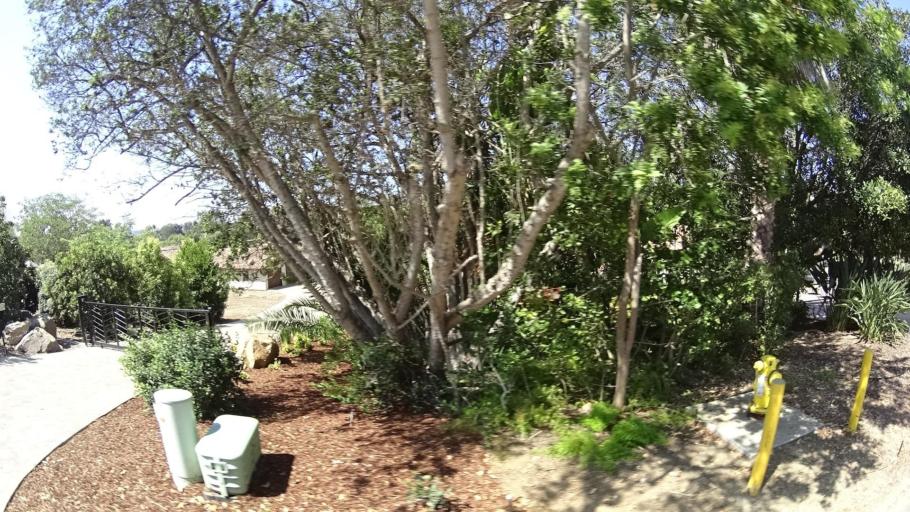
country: US
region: California
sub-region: San Diego County
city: Rancho Santa Fe
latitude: 33.0174
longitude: -117.1891
